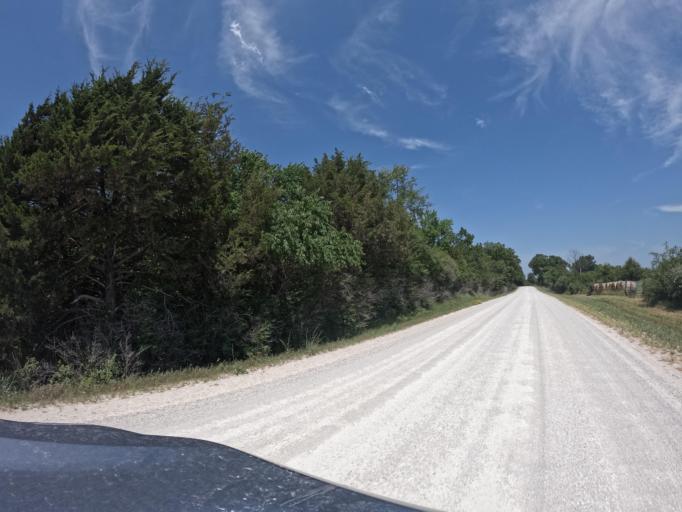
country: US
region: Iowa
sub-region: Henry County
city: Mount Pleasant
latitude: 40.9076
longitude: -91.5469
